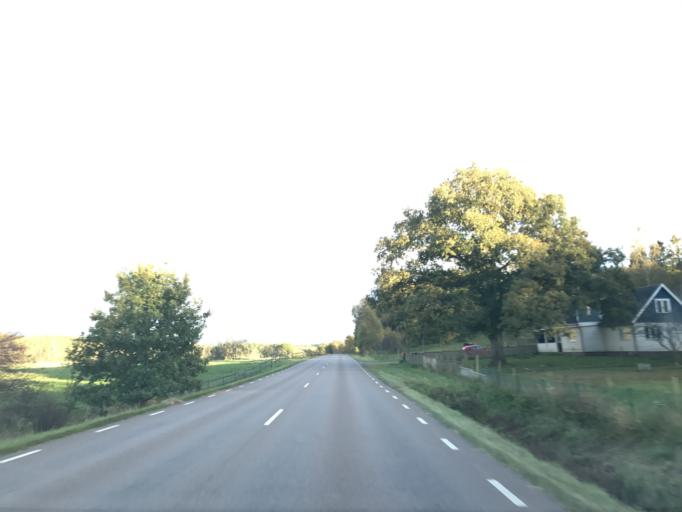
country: SE
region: Skane
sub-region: Klippans Kommun
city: Ljungbyhed
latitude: 56.1405
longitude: 13.2735
